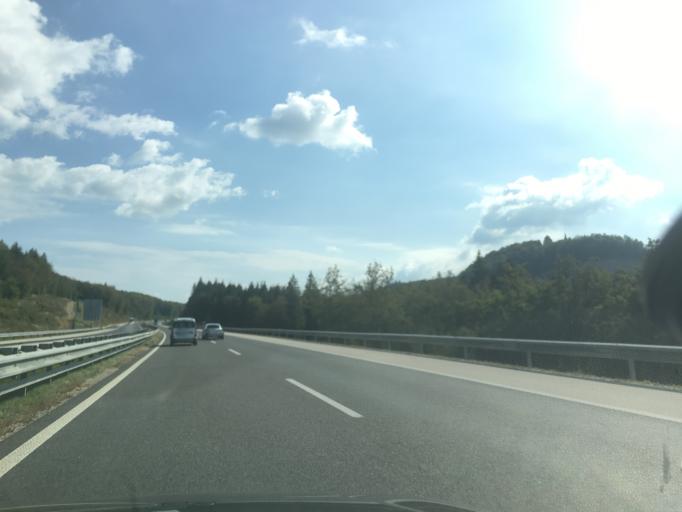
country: SI
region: Mirna Pec
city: Mirna Pec
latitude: 45.8892
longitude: 15.0634
